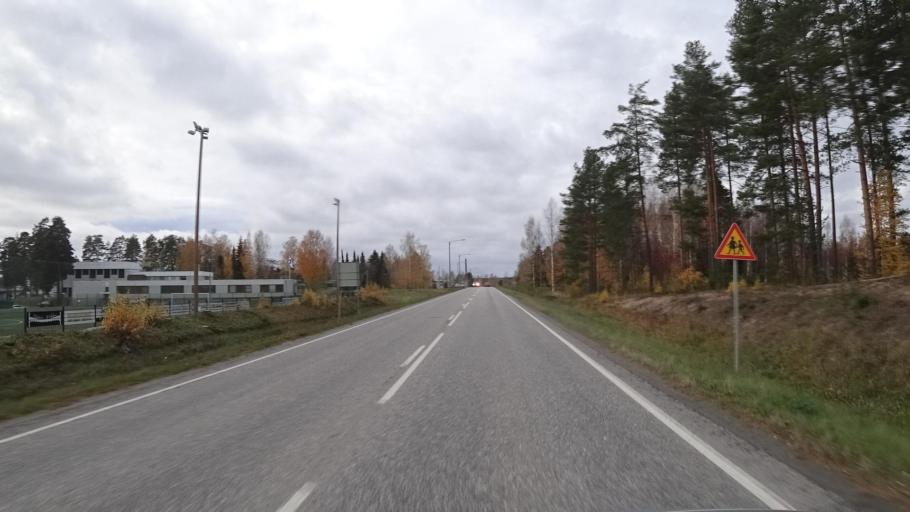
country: FI
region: Central Finland
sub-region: Joutsa
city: Joutsa
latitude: 61.7487
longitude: 26.1261
